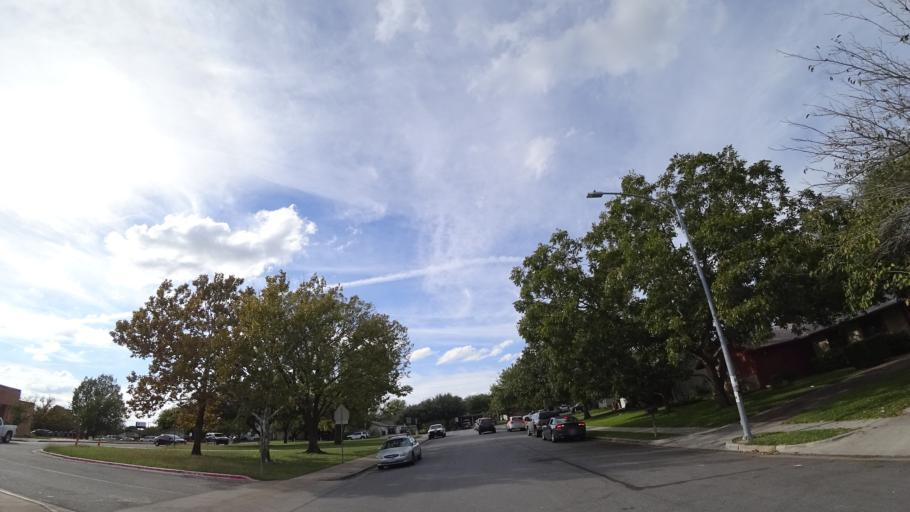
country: US
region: Texas
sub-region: Travis County
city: Onion Creek
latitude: 30.1983
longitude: -97.7546
